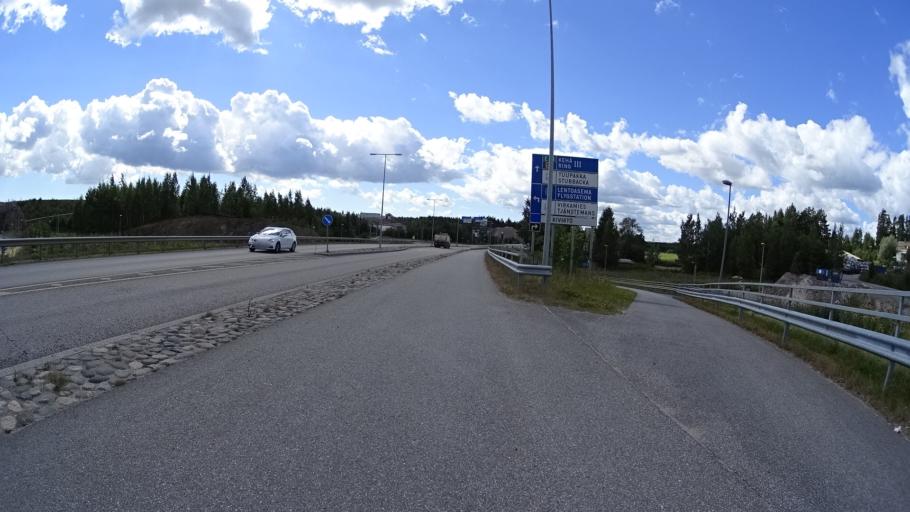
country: FI
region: Uusimaa
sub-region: Helsinki
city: Teekkarikylae
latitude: 60.3096
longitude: 24.8904
